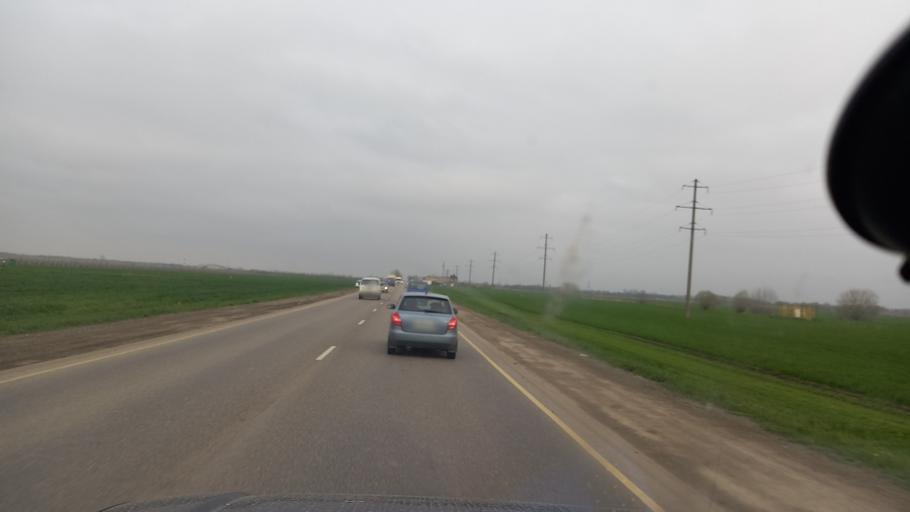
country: RU
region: Krasnodarskiy
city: Slavyansk-na-Kubani
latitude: 45.2414
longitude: 38.0271
